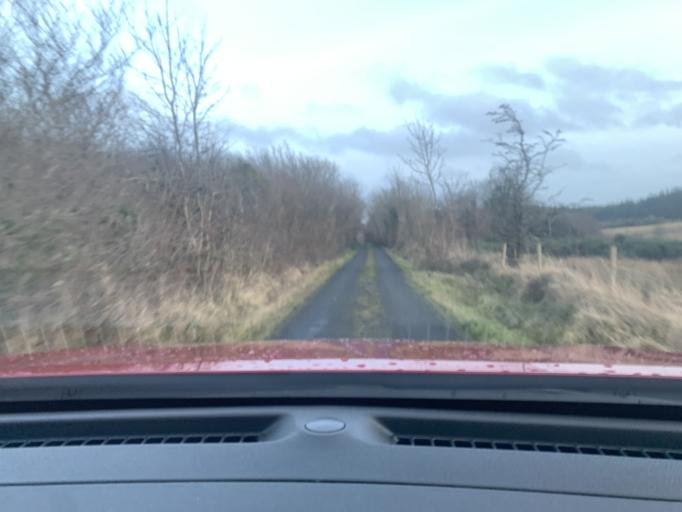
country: IE
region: Connaught
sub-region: Sligo
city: Ballymote
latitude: 53.9911
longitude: -8.4521
